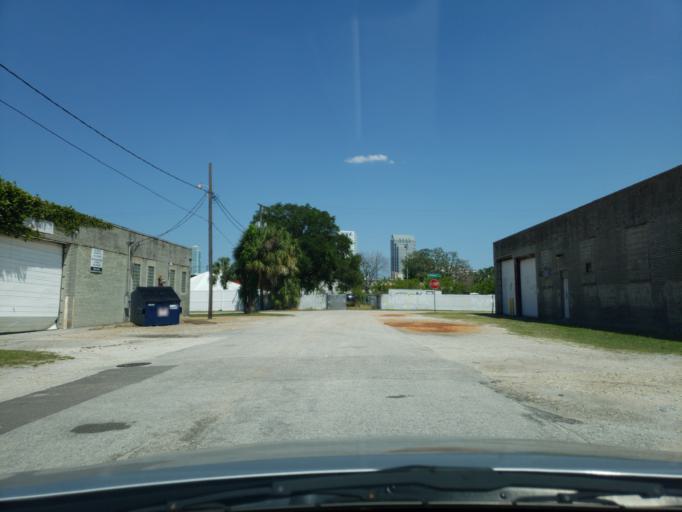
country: US
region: Florida
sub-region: Hillsborough County
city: Tampa
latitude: 27.9468
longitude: -82.4723
